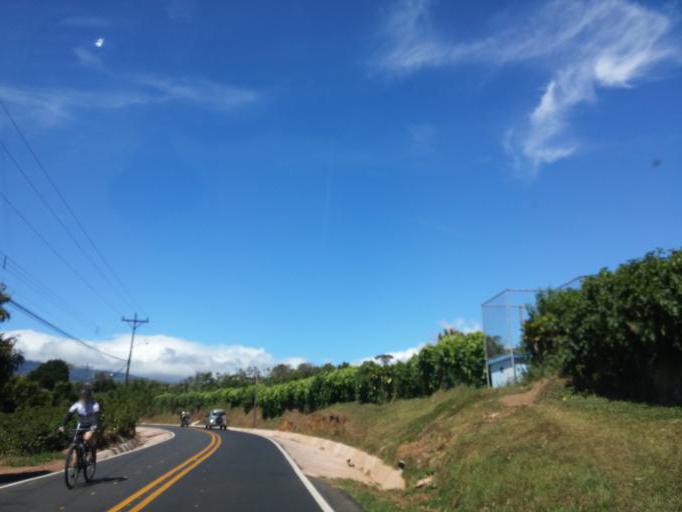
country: CR
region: Alajuela
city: Sabanilla
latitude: 10.0832
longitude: -84.1903
